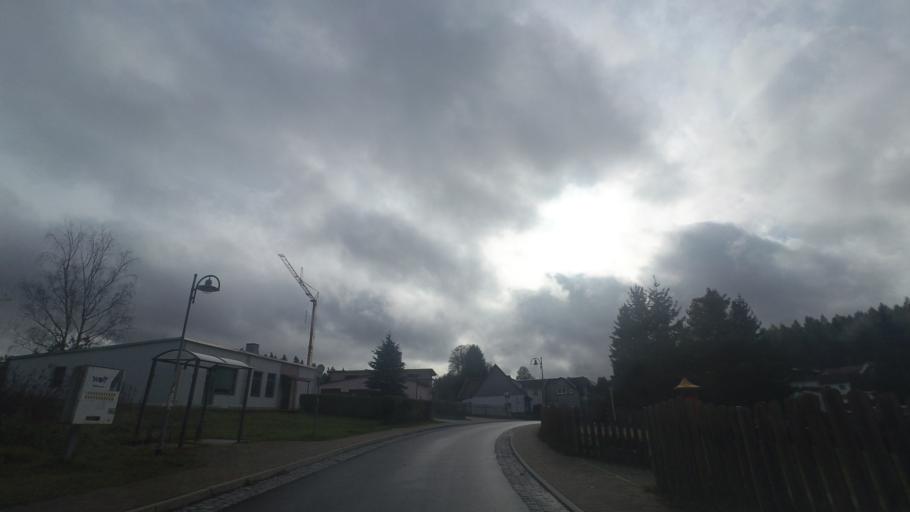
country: DE
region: Thuringia
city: Schleusingen
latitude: 50.4835
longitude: 10.8292
